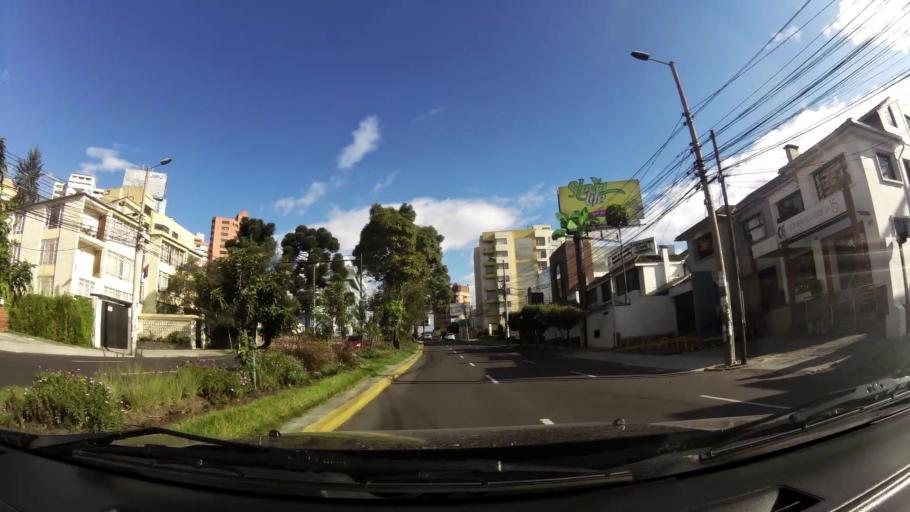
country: EC
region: Pichincha
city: Quito
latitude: -0.2009
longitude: -78.4829
